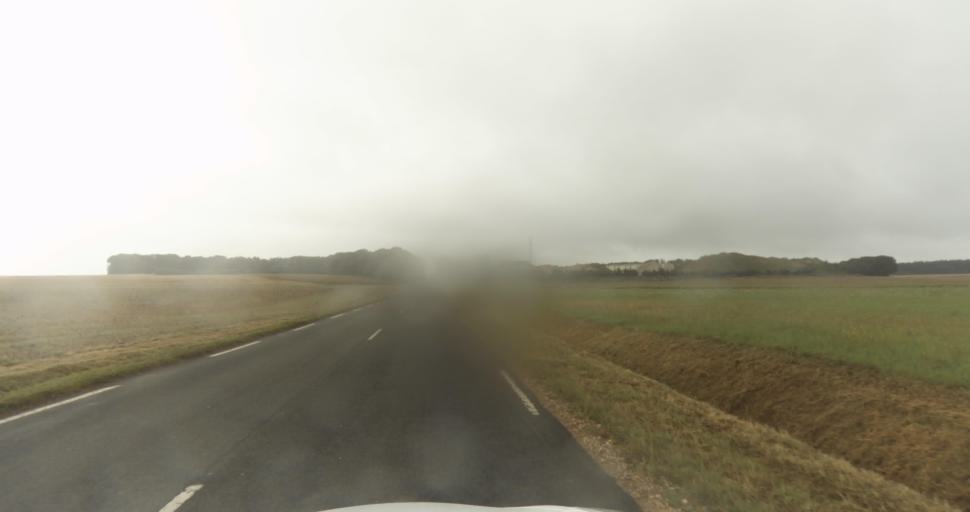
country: FR
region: Haute-Normandie
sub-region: Departement de l'Eure
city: Normanville
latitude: 49.0970
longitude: 1.1746
